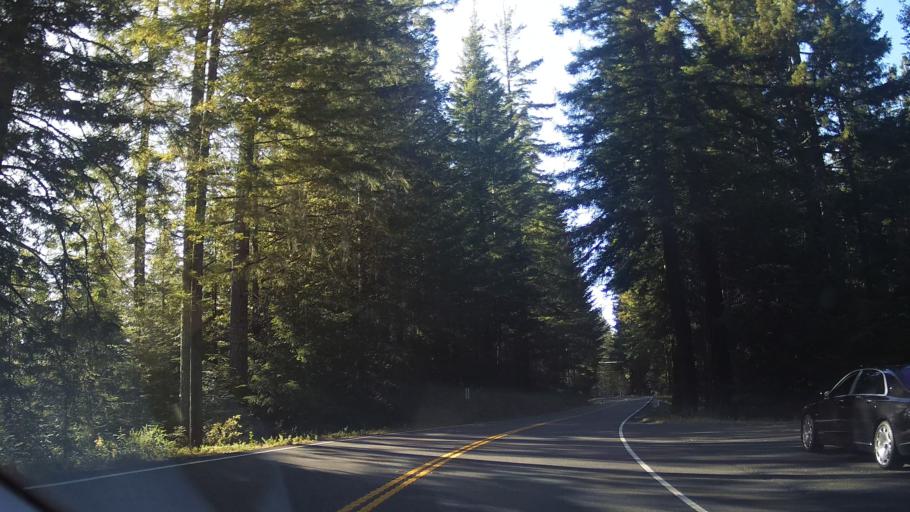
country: US
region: California
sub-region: Mendocino County
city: Fort Bragg
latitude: 39.3787
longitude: -123.6908
